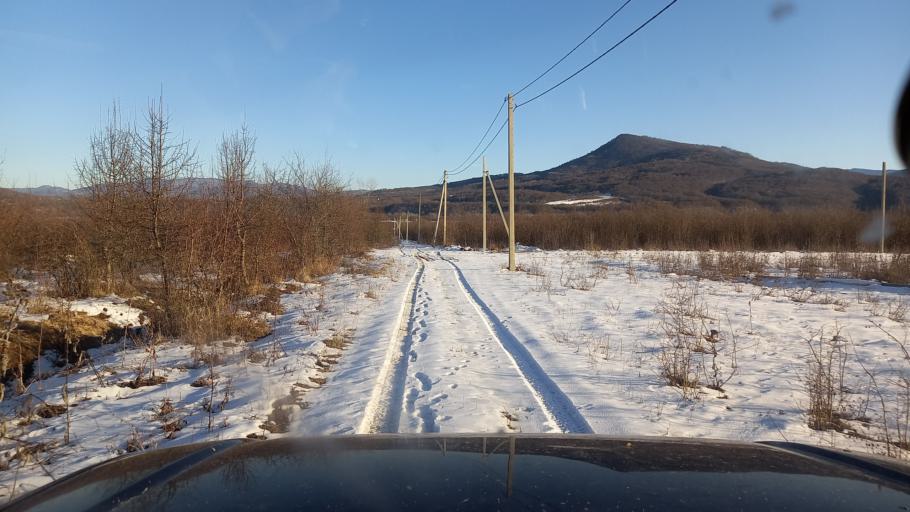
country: RU
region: Adygeya
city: Kamennomostskiy
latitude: 44.2258
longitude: 40.1689
